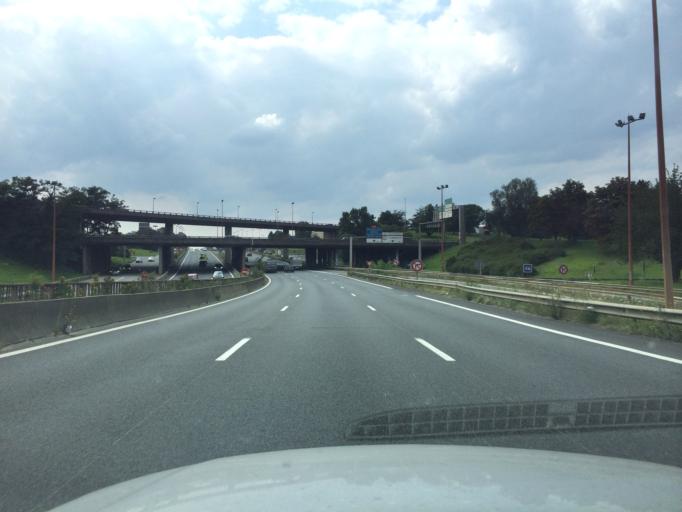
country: FR
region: Ile-de-France
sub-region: Departement de l'Essonne
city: Bievres
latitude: 48.7772
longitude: 2.2245
